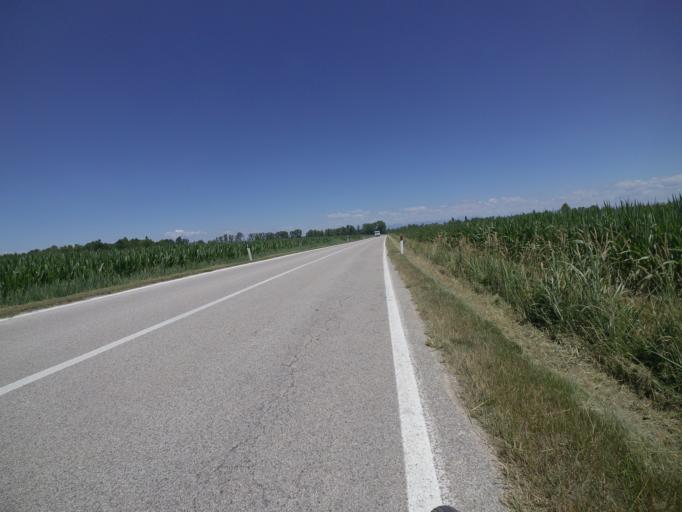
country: IT
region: Friuli Venezia Giulia
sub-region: Provincia di Udine
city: Bertiolo
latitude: 45.9093
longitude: 13.0813
